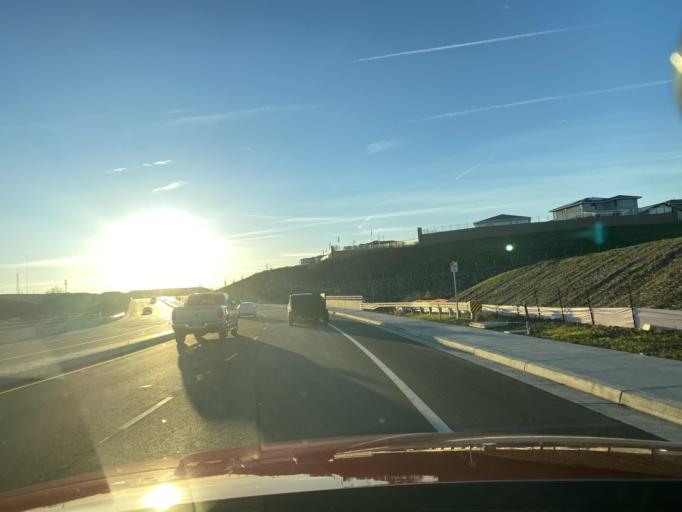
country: US
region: California
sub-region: El Dorado County
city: El Dorado Hills
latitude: 38.6510
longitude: -121.0804
